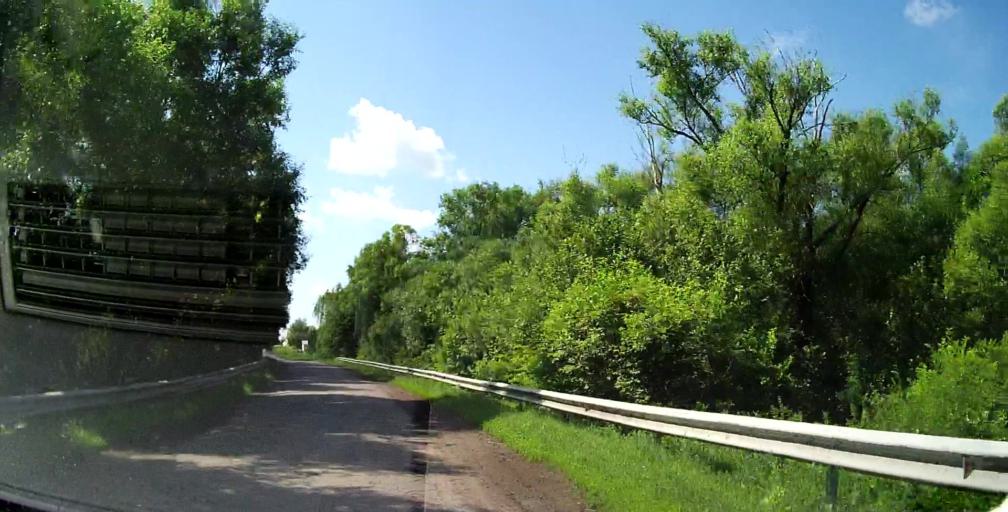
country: RU
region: Lipetsk
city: Chaplygin
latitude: 53.3715
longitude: 39.9164
